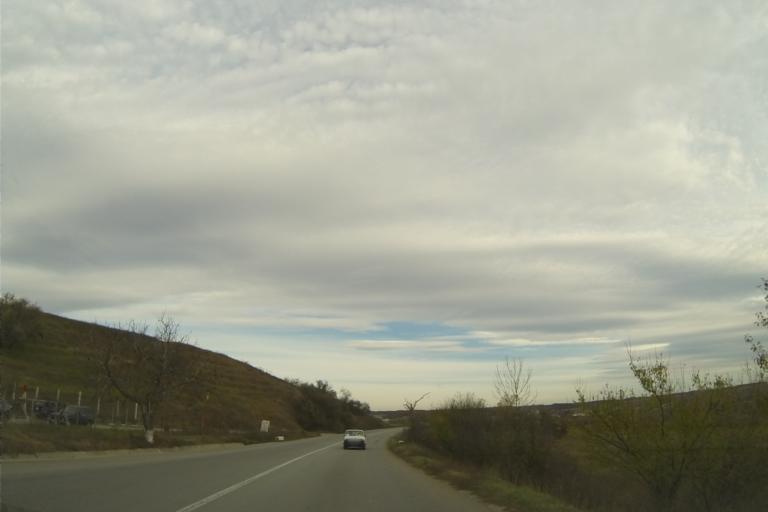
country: RO
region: Olt
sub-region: Comuna Scornicesti
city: Scornicesti
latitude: 44.5490
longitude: 24.5512
